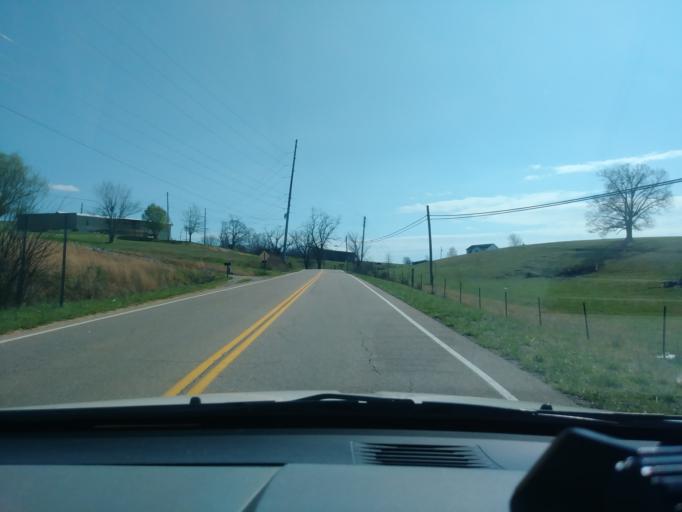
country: US
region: Tennessee
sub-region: Greene County
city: Tusculum
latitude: 36.1130
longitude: -82.7757
